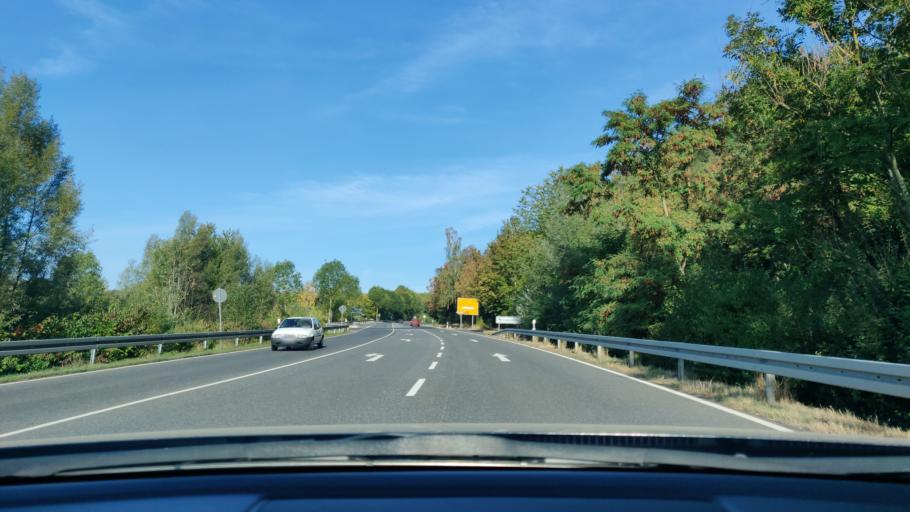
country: DE
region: Hesse
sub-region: Regierungsbezirk Kassel
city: Bad Wildungen
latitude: 51.1287
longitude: 9.1550
